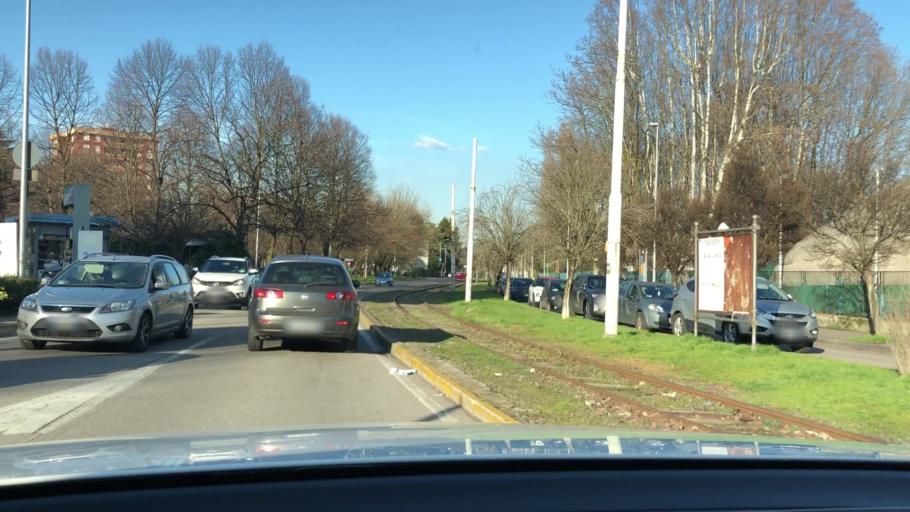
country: IT
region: Lombardy
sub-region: Citta metropolitana di Milano
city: Cusano Milanino
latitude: 45.5535
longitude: 9.1862
